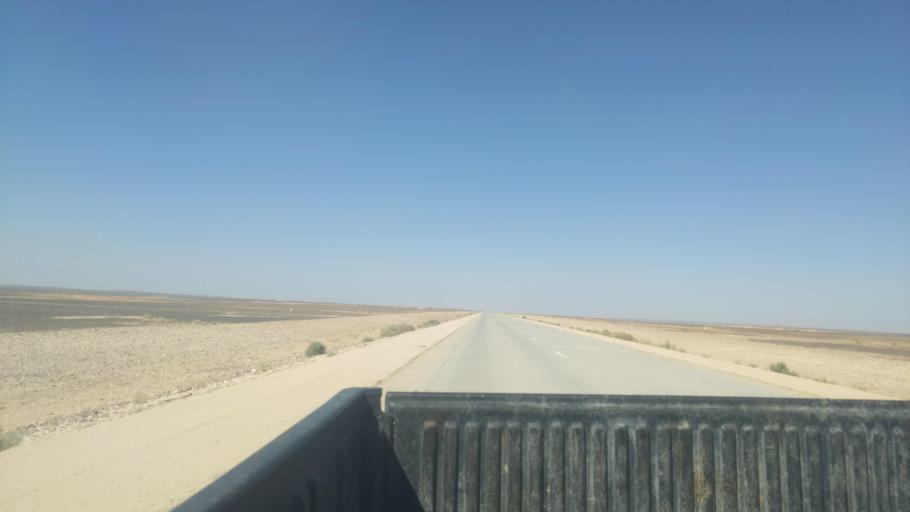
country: JO
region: Amman
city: Al Azraq ash Shamali
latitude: 31.4563
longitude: 36.7849
